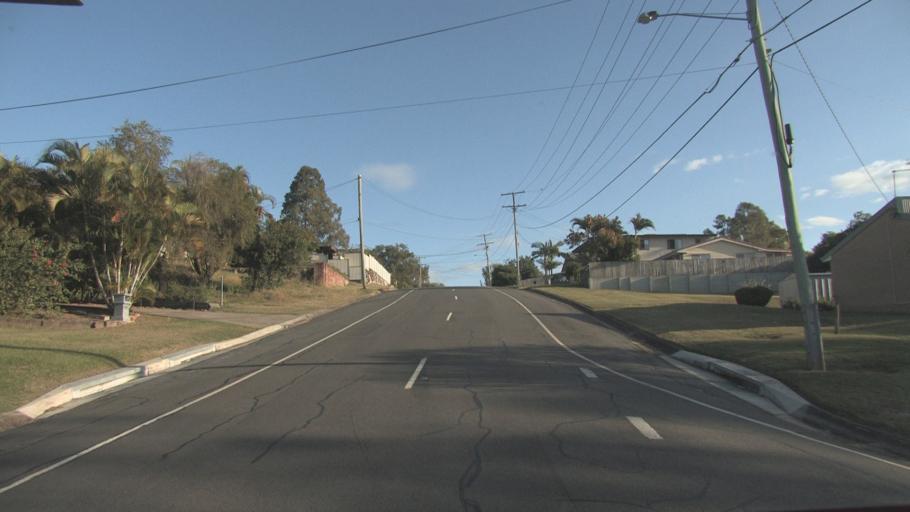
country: AU
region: Queensland
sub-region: Logan
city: Beenleigh
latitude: -27.7073
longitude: 153.1770
